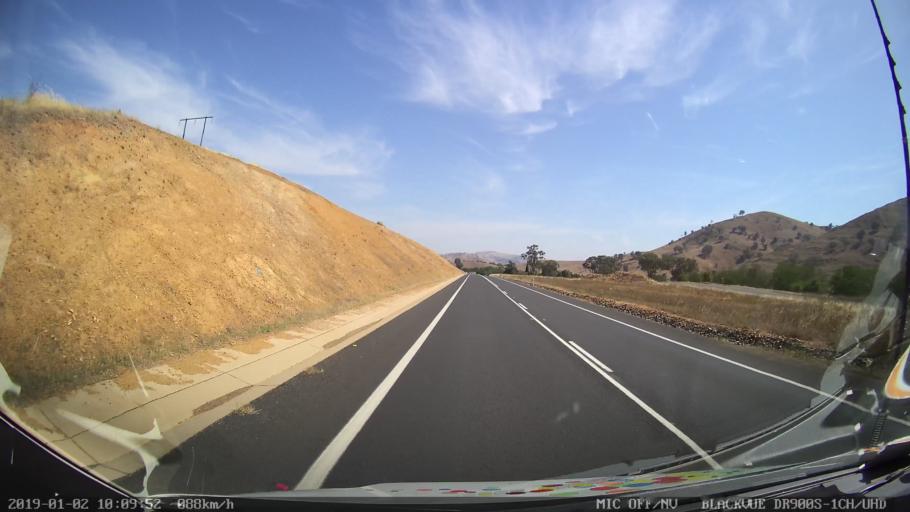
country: AU
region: New South Wales
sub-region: Gundagai
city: Gundagai
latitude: -35.1118
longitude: 148.0974
